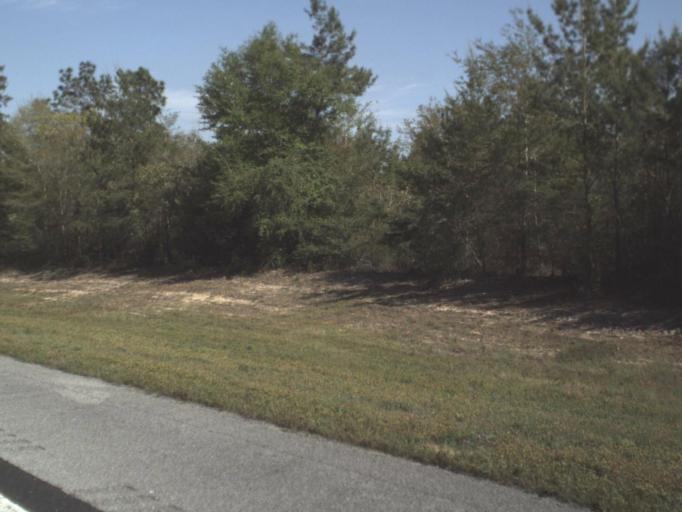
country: US
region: Florida
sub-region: Okaloosa County
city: Crestview
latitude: 30.7126
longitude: -86.6998
